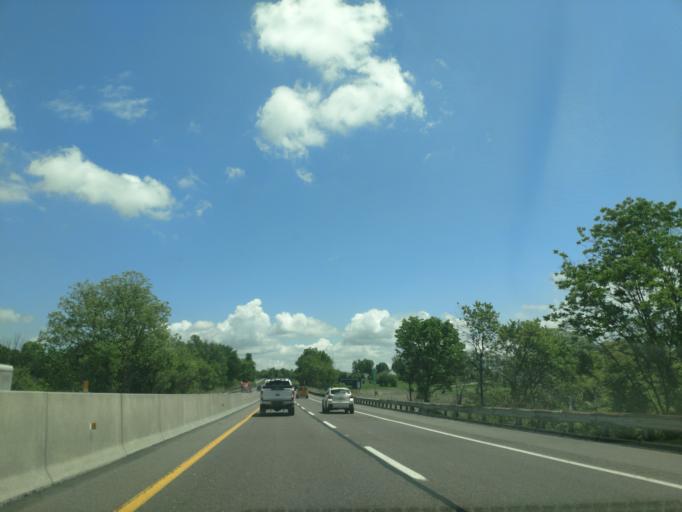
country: US
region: Pennsylvania
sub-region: Chester County
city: Elverson
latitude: 40.1435
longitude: -75.8125
